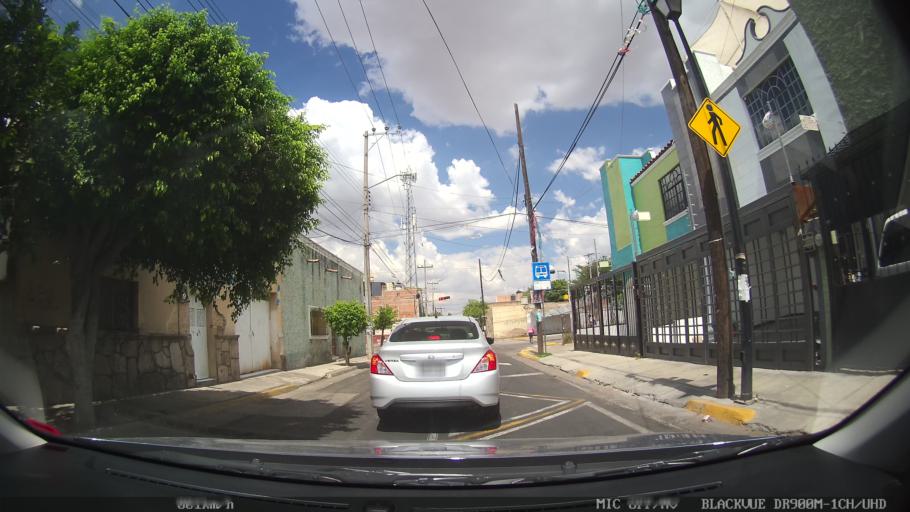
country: MX
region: Jalisco
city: Tlaquepaque
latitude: 20.6588
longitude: -103.2750
